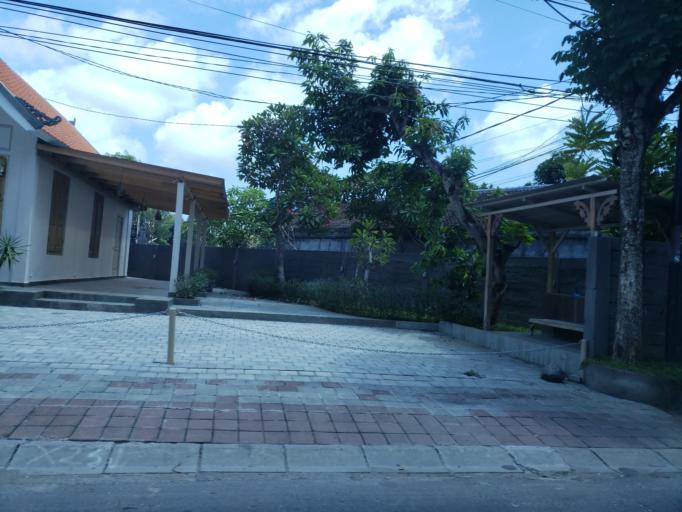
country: ID
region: Bali
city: Jimbaran
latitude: -8.7831
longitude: 115.1668
